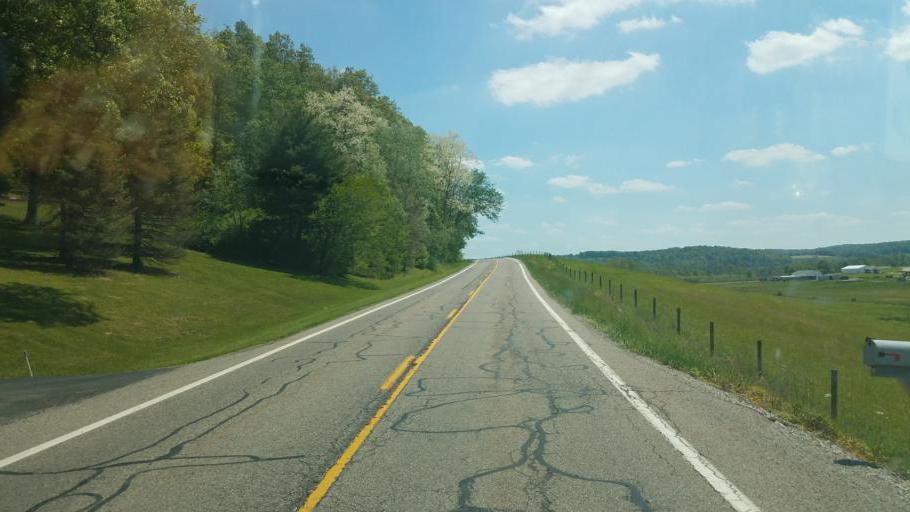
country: US
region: Ohio
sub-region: Muskingum County
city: Frazeysburg
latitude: 40.1433
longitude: -82.2137
